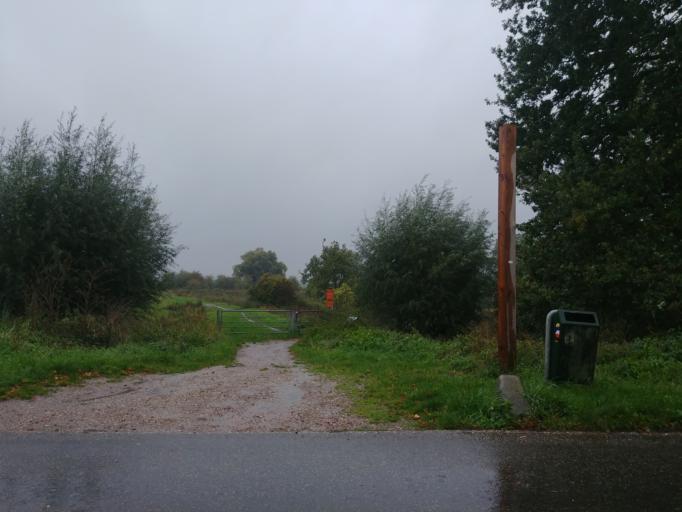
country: NL
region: Gelderland
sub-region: Gemeente Renkum
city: Renkum
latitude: 51.9720
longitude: 5.7350
